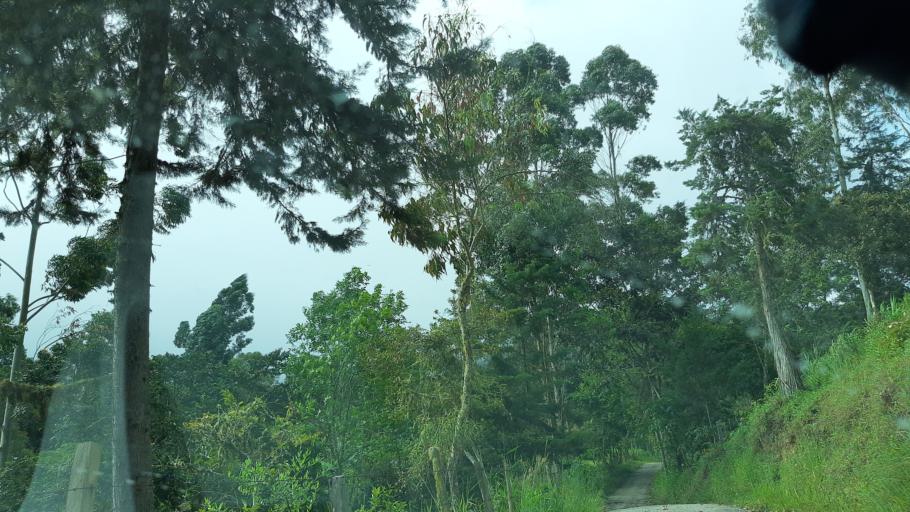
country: CO
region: Boyaca
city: Garagoa
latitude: 5.0380
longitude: -73.3471
